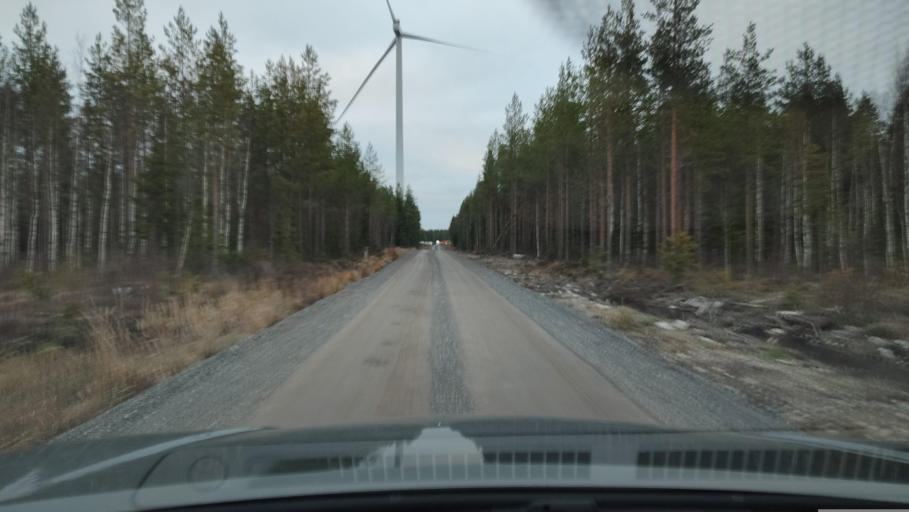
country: FI
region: Southern Ostrobothnia
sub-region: Suupohja
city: Karijoki
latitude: 62.1842
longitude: 21.5621
